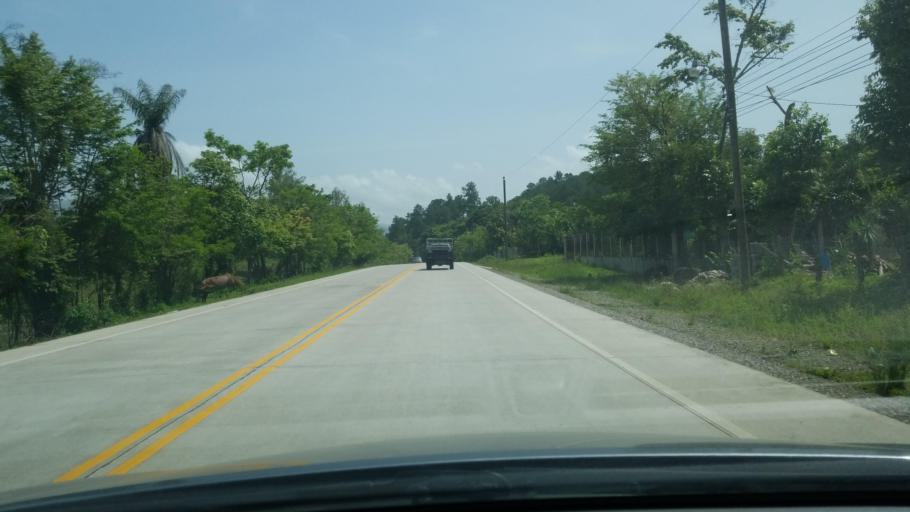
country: HN
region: Copan
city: Florida
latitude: 15.0061
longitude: -88.8361
